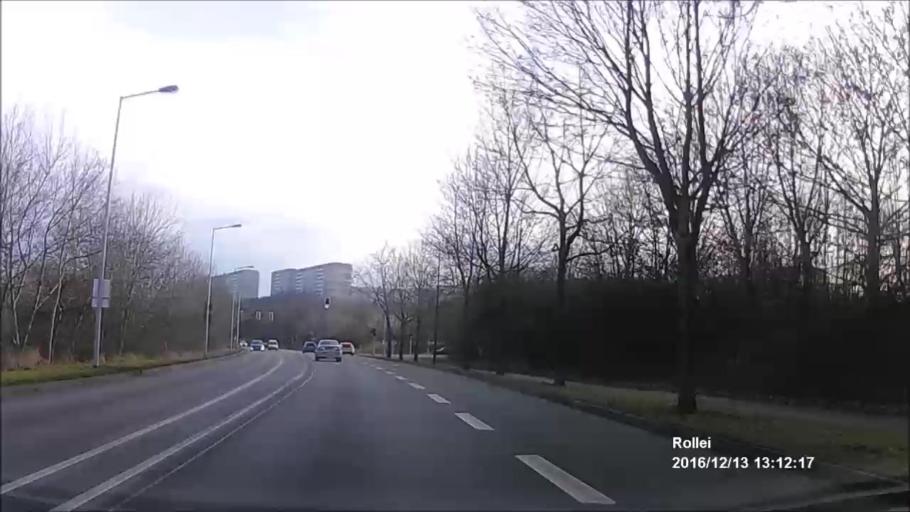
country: DE
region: Thuringia
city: Erfurt
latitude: 50.9611
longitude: 11.0633
